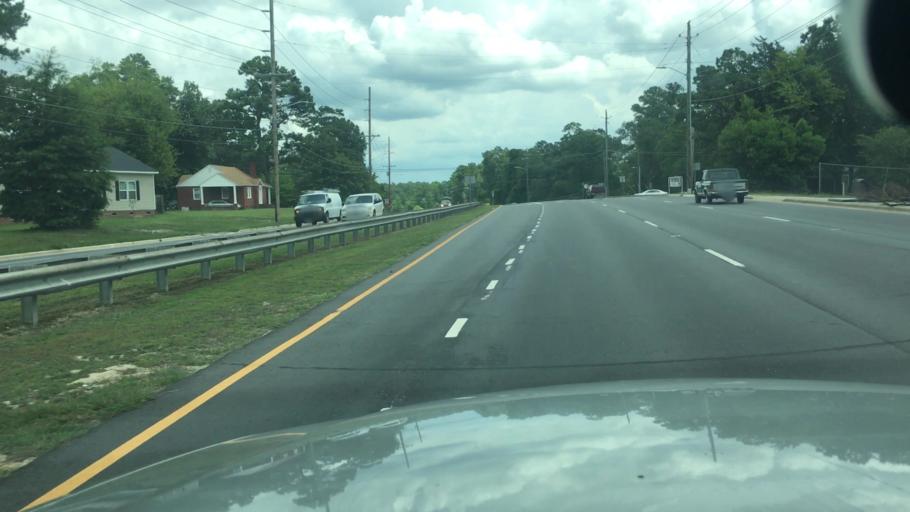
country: US
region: North Carolina
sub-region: Cumberland County
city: Fayetteville
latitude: 35.0702
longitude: -78.9182
